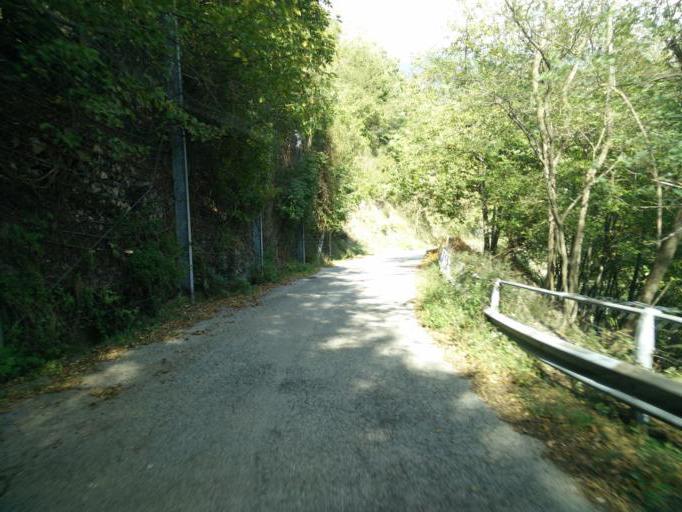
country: IT
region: Tuscany
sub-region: Provincia di Massa-Carrara
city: Patigno
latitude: 44.3497
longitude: 9.7134
